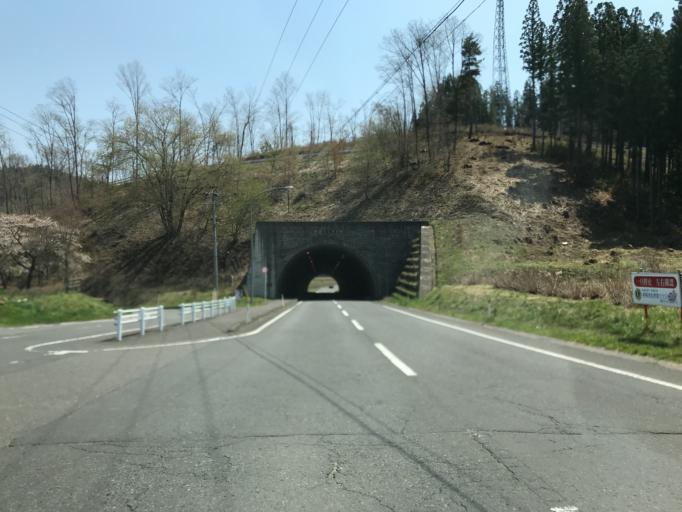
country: JP
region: Fukushima
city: Ishikawa
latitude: 37.0403
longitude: 140.5062
